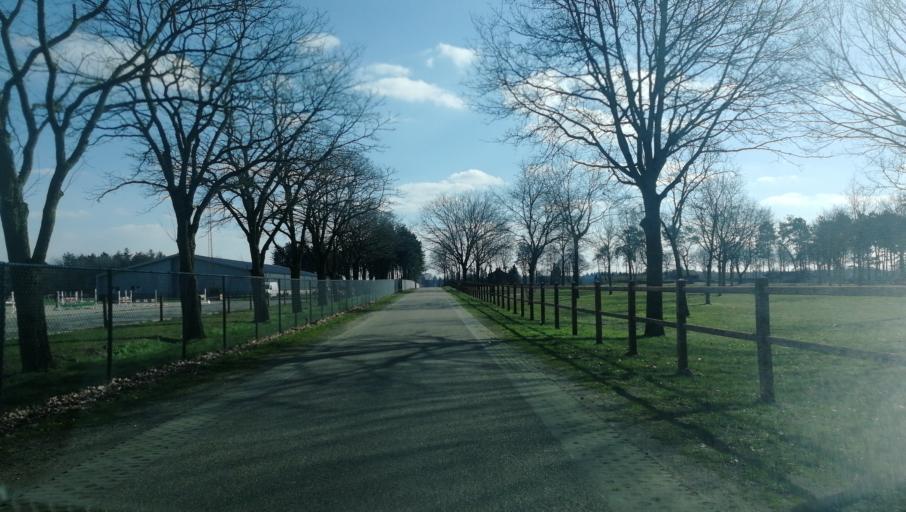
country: NL
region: Limburg
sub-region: Gemeente Peel en Maas
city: Maasbree
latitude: 51.4097
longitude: 5.9687
